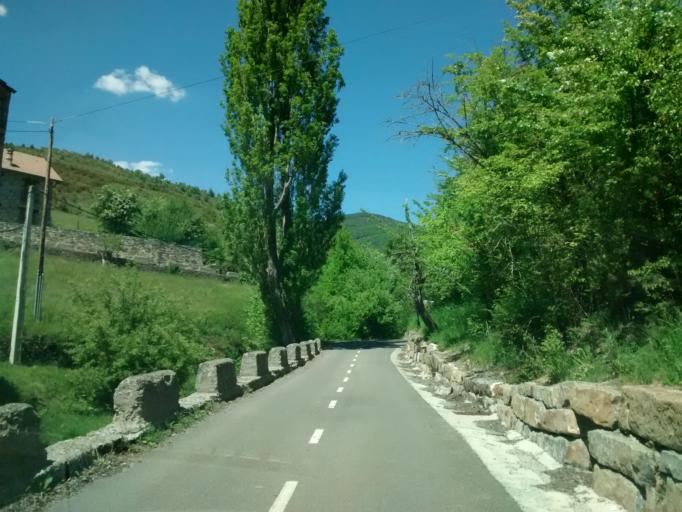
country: ES
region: Aragon
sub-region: Provincia de Huesca
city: Borau
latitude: 42.6587
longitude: -0.5866
